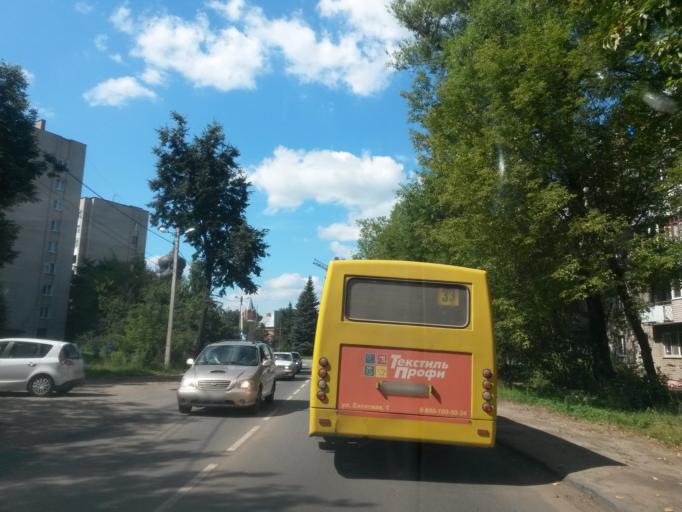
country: RU
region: Ivanovo
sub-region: Gorod Ivanovo
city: Ivanovo
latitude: 57.0100
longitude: 40.9936
